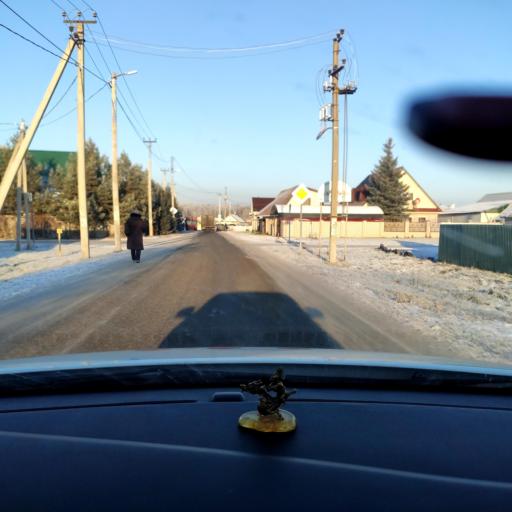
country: RU
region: Tatarstan
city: Stolbishchi
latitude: 55.6752
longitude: 49.1171
